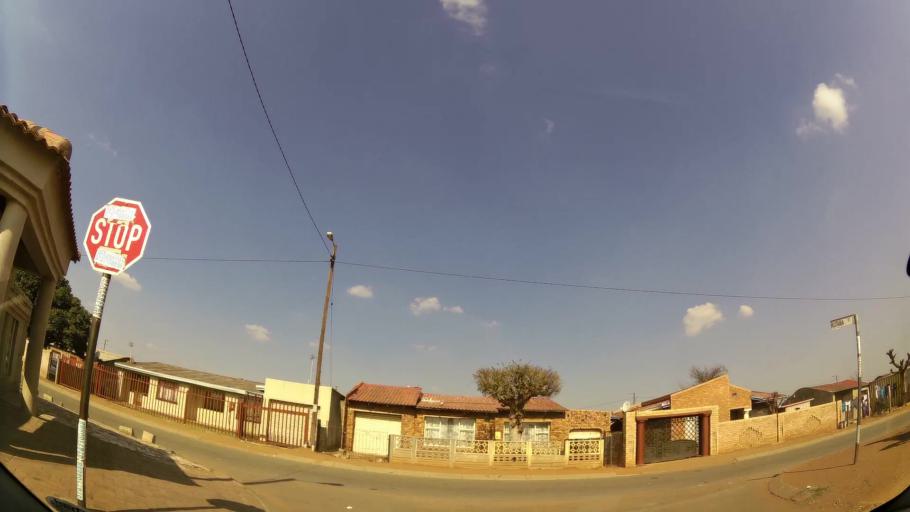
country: ZA
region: Gauteng
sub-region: Ekurhuleni Metropolitan Municipality
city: Brakpan
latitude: -26.1513
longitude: 28.4112
